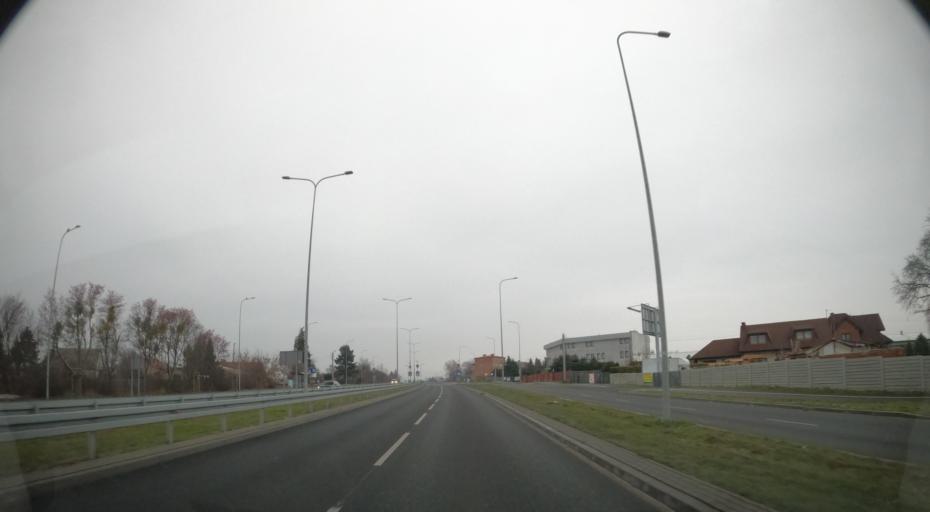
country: PL
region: Masovian Voivodeship
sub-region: Radom
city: Radom
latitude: 51.3837
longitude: 21.1848
